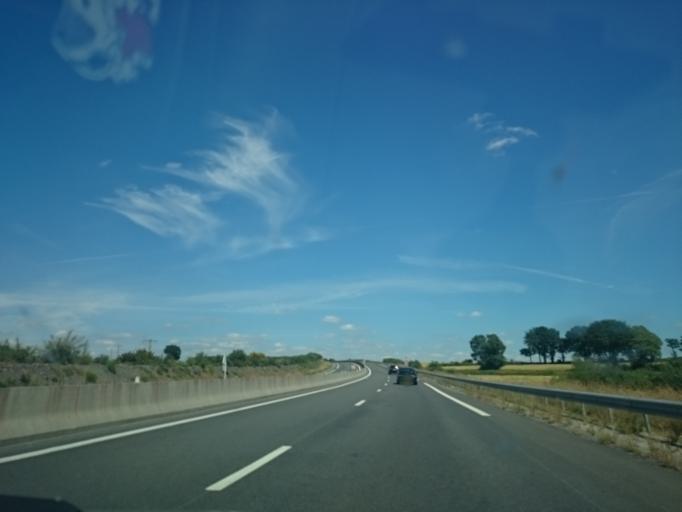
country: FR
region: Brittany
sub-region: Departement des Cotes-d'Armor
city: Gouarec
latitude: 48.2314
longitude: -3.1571
